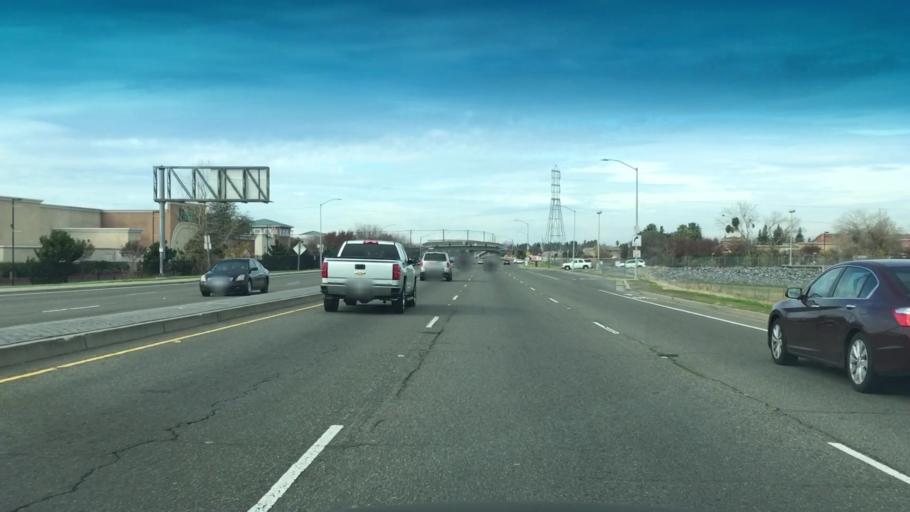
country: US
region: California
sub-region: Sacramento County
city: Laguna
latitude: 38.4570
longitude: -121.4137
